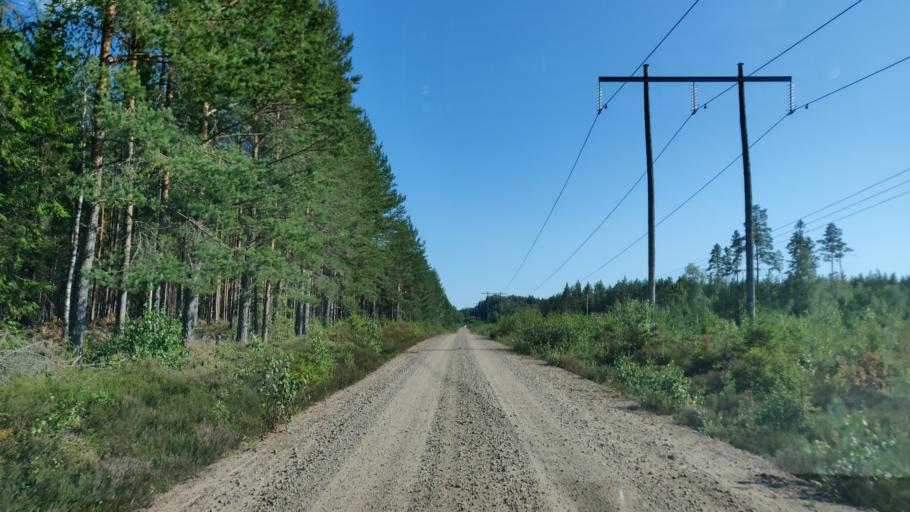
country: SE
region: Vaermland
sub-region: Hagfors Kommun
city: Ekshaerad
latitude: 60.0533
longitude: 13.5222
